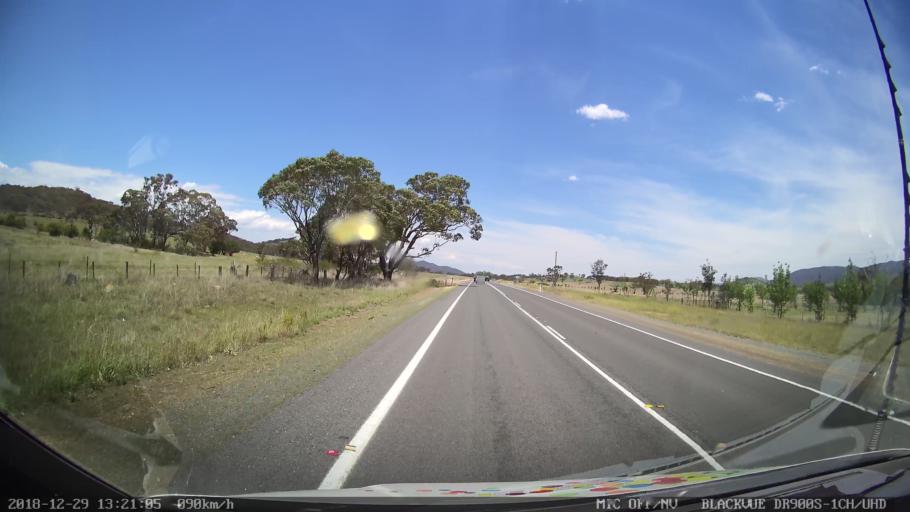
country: AU
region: Australian Capital Territory
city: Macarthur
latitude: -35.7874
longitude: 149.1631
